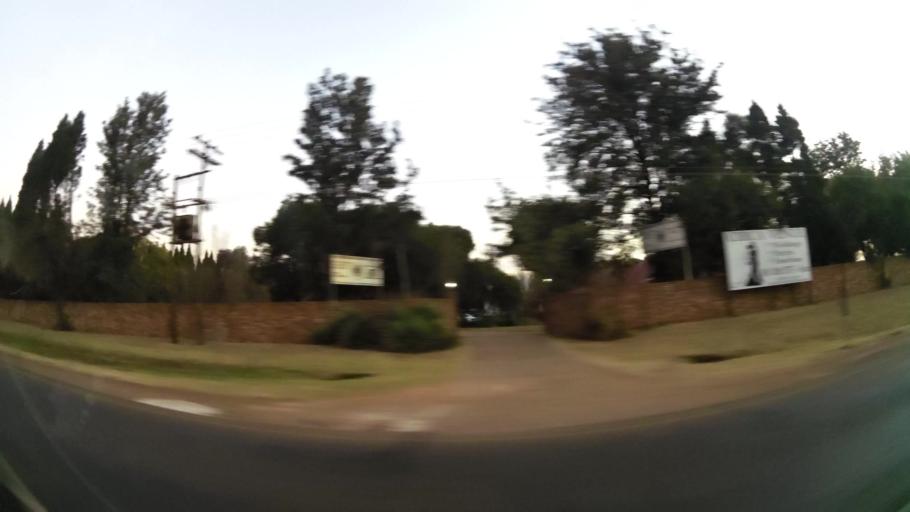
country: ZA
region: Gauteng
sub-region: West Rand District Municipality
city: Randfontein
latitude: -26.0856
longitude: 27.6640
